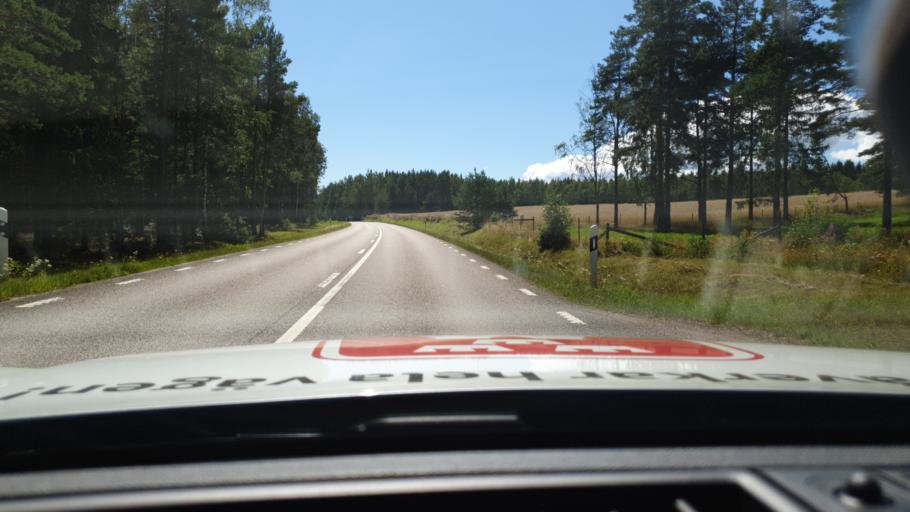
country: SE
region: Vaestra Goetaland
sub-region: Hjo Kommun
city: Hjo
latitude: 58.1897
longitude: 14.2034
